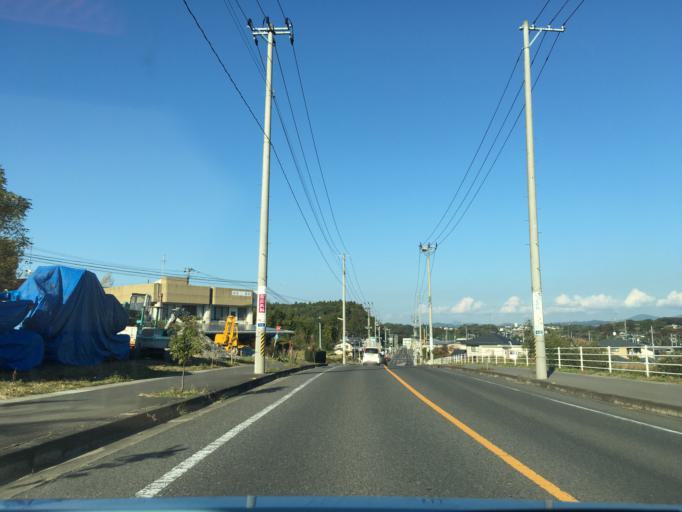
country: JP
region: Fukushima
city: Sukagawa
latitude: 37.3061
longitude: 140.3721
